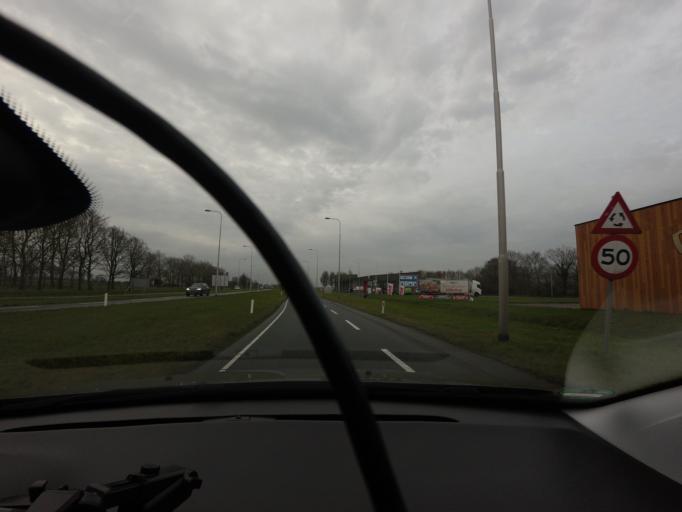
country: NL
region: North Holland
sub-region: Gemeente Hollands Kroon
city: Den Oever
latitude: 52.9291
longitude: 5.0299
